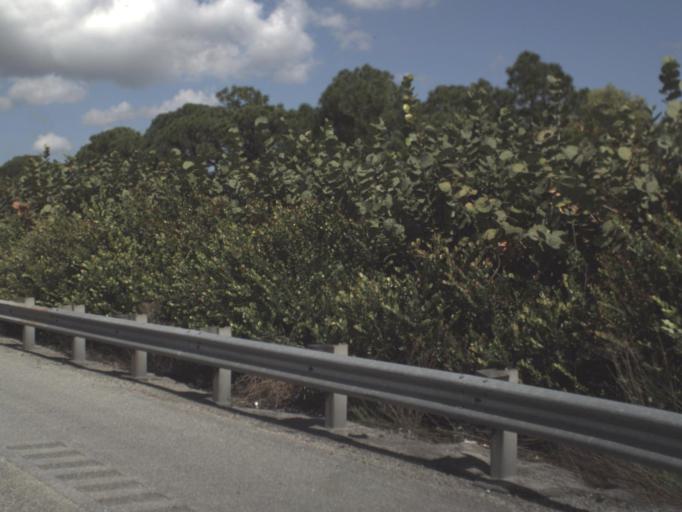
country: US
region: Florida
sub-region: Palm Beach County
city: Limestone Creek
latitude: 26.9219
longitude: -80.1481
